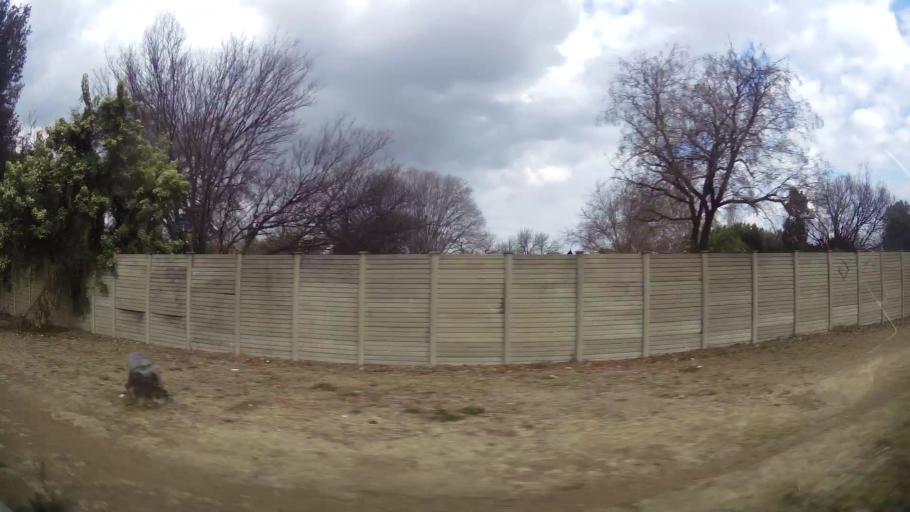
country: ZA
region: Orange Free State
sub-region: Fezile Dabi District Municipality
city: Sasolburg
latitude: -26.8047
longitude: 27.8308
